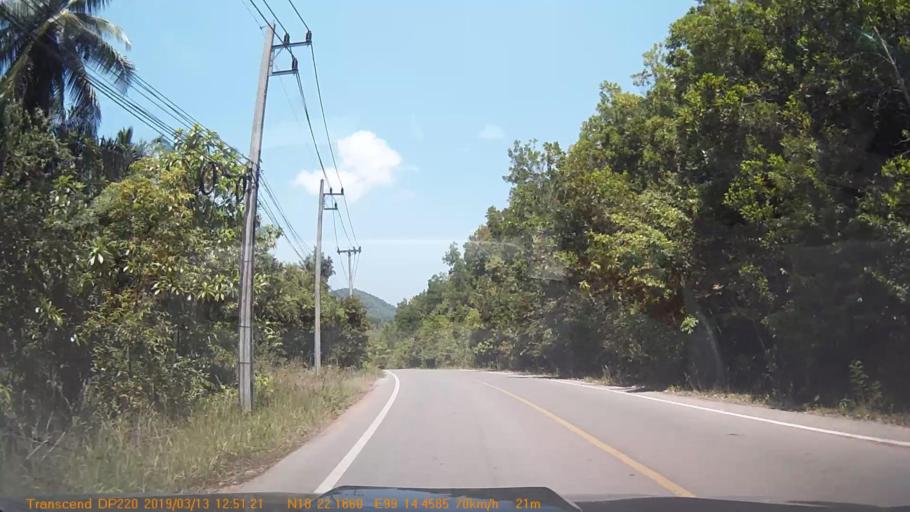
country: TH
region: Chumphon
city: Chumphon
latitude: 10.3700
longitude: 99.2412
